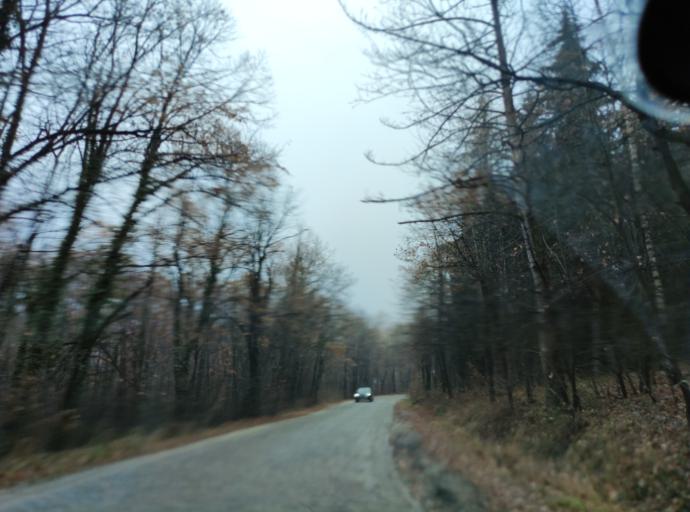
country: BG
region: Sofia-Capital
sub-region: Stolichna Obshtina
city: Sofia
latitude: 42.6218
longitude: 23.3068
